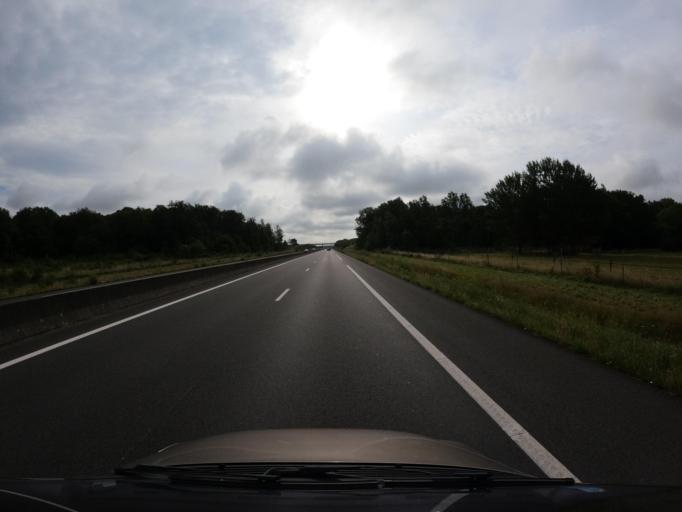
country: FR
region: Centre
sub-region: Departement d'Indre-et-Loire
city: Monts
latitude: 47.3076
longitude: 0.6123
